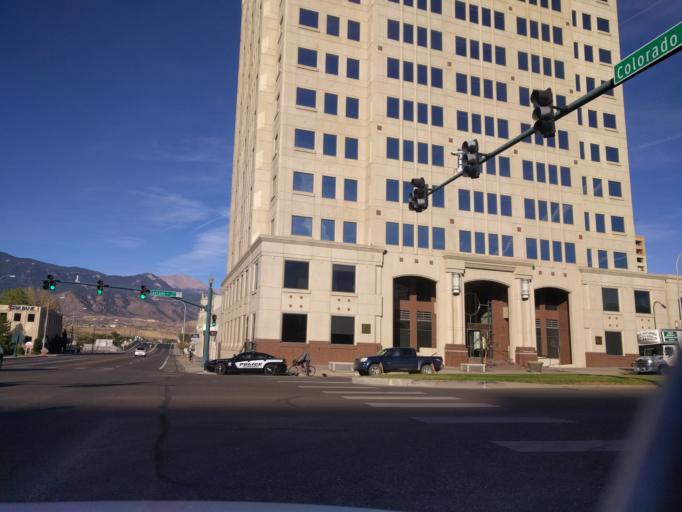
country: US
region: Colorado
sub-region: El Paso County
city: Colorado Springs
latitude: 38.8326
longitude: -104.8252
